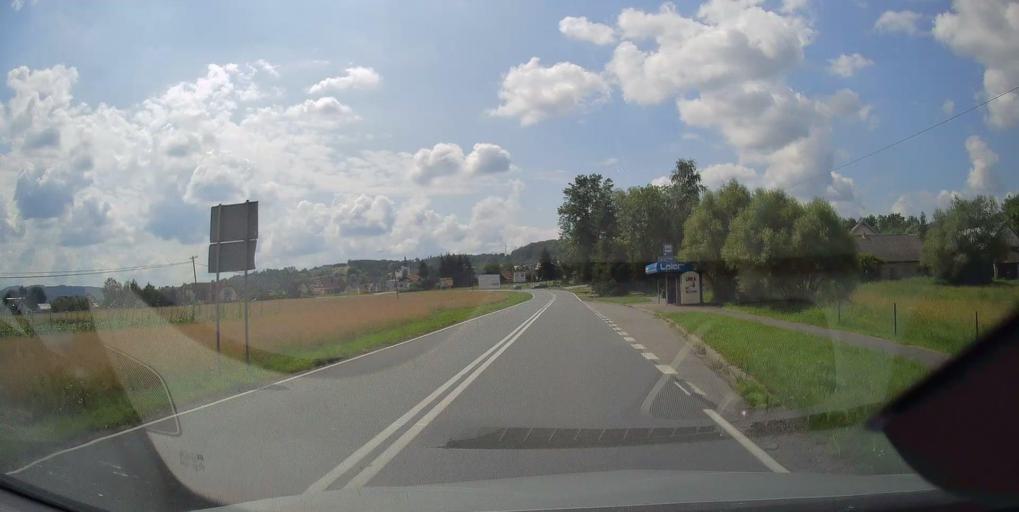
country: PL
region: Lesser Poland Voivodeship
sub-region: Powiat tarnowski
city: Zakliczyn
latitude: 49.8935
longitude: 20.8172
